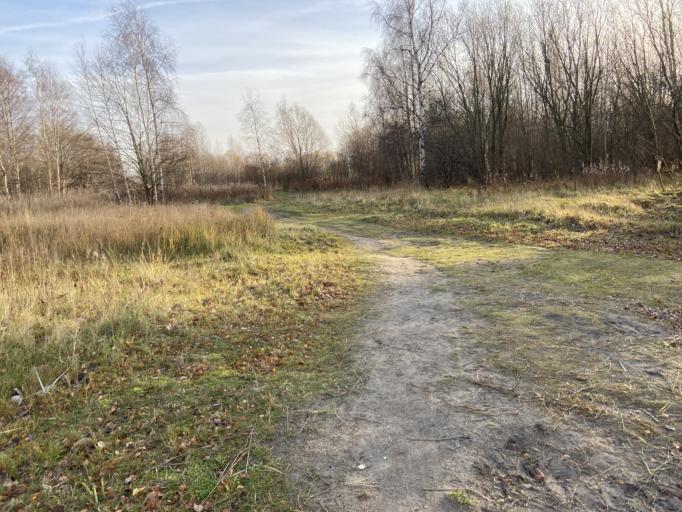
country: EE
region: Harju
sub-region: Tallinna linn
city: Tallinn
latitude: 59.4752
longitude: 24.7191
